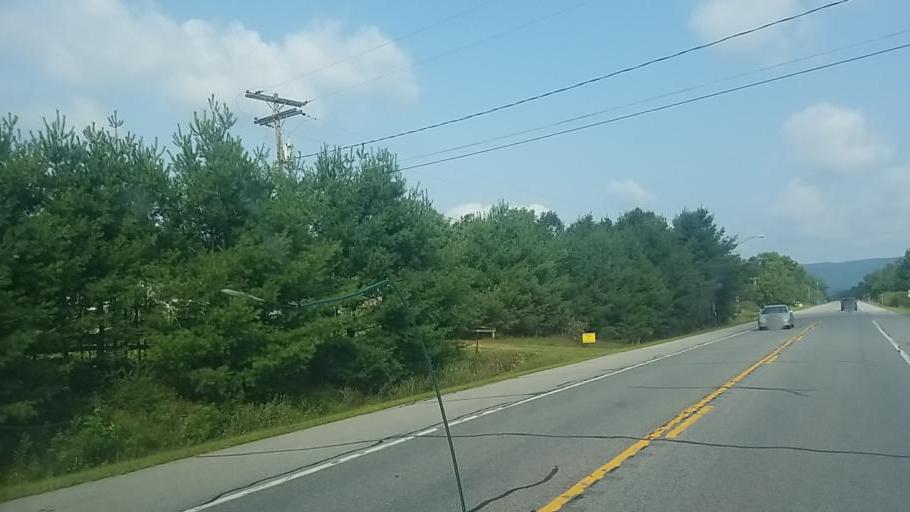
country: US
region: New York
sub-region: Fulton County
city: Broadalbin
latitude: 43.0789
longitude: -74.2618
